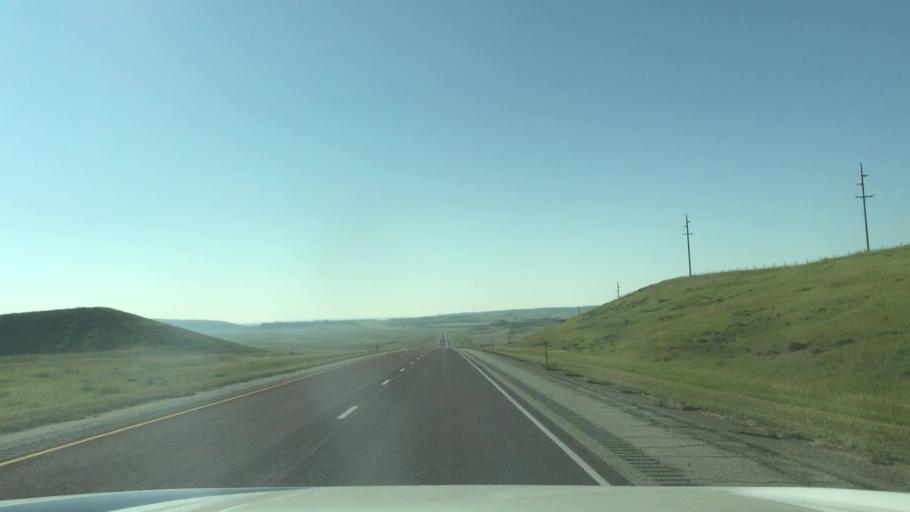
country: US
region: Wyoming
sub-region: Converse County
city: Douglas
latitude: 42.6246
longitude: -105.1410
